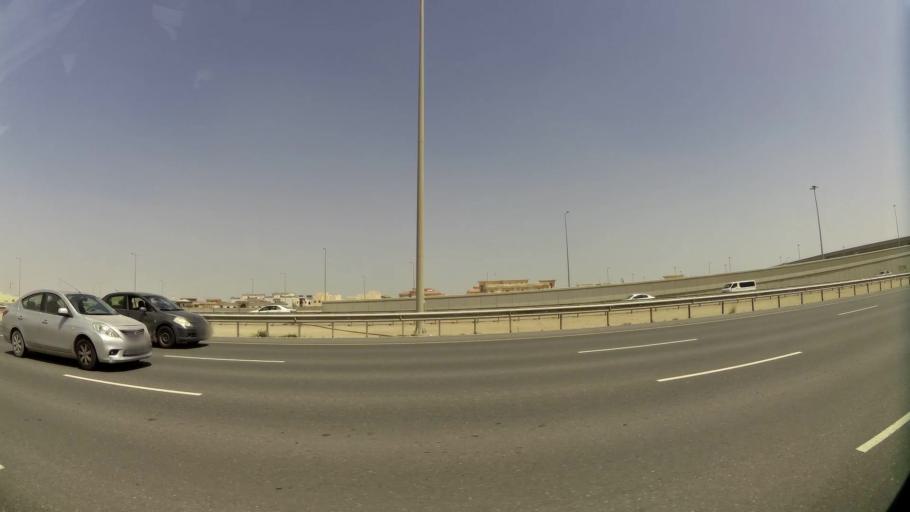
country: QA
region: Baladiyat Umm Salal
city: Umm Salal Muhammad
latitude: 25.3668
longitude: 51.4467
